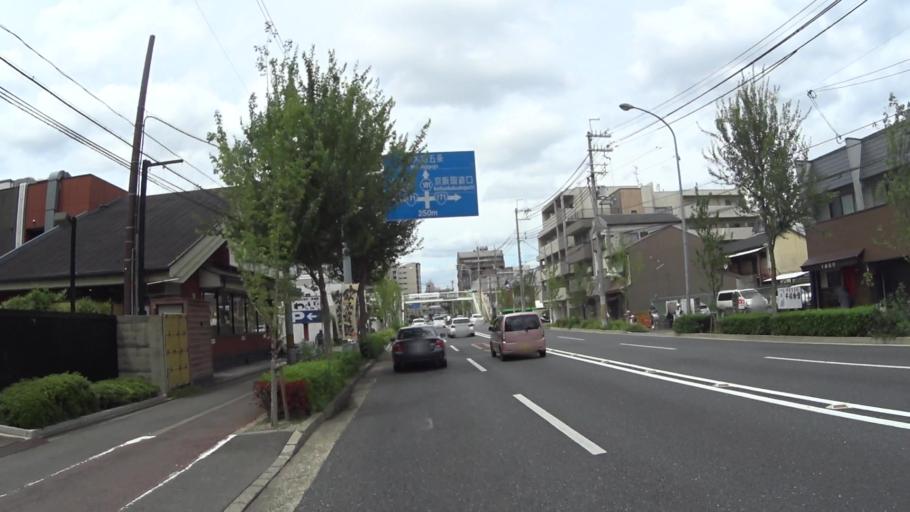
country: JP
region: Kyoto
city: Muko
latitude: 34.9760
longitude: 135.7344
